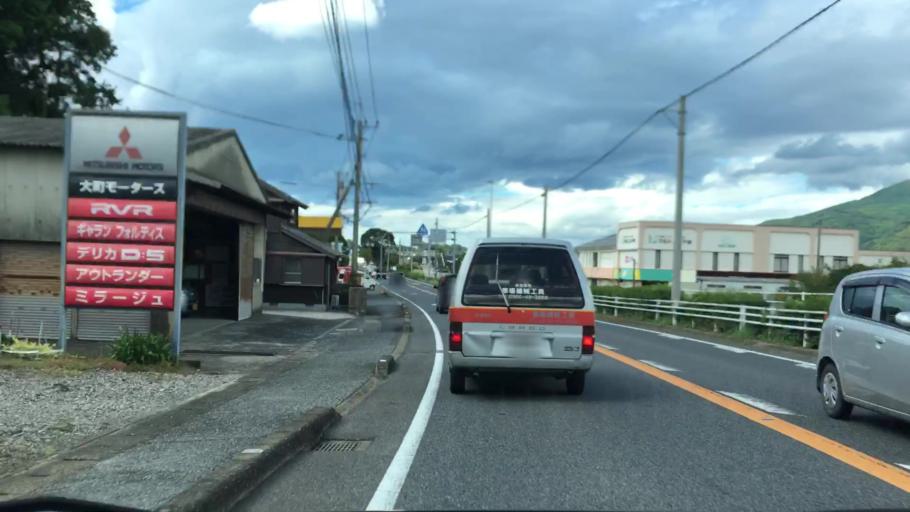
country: JP
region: Saga Prefecture
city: Imaricho-ko
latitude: 33.2064
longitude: 129.8505
